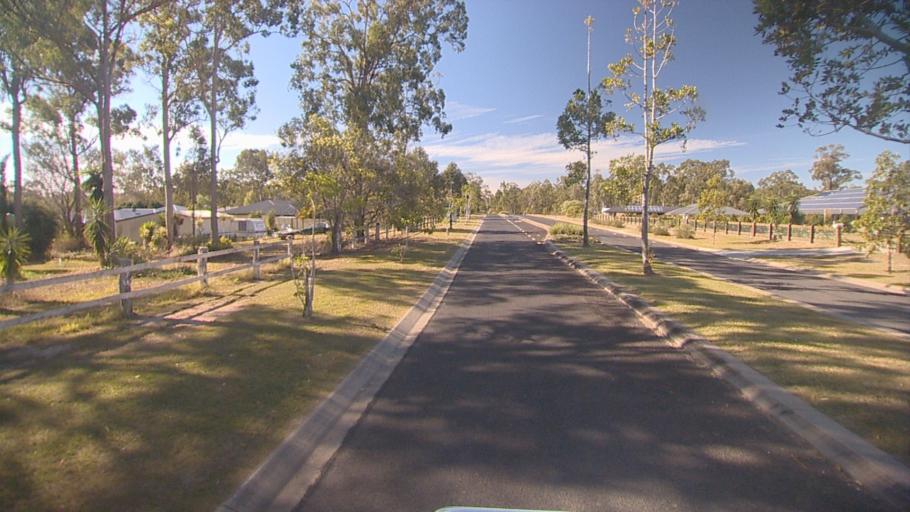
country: AU
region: Queensland
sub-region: Ipswich
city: Springfield Lakes
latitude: -27.7354
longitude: 152.9201
